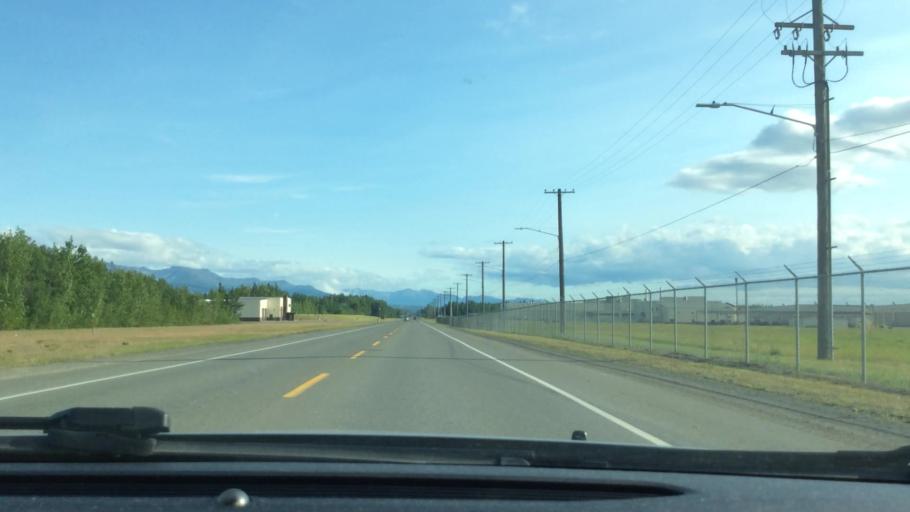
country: US
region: Alaska
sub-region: Anchorage Municipality
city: Anchorage
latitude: 61.2494
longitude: -149.7792
